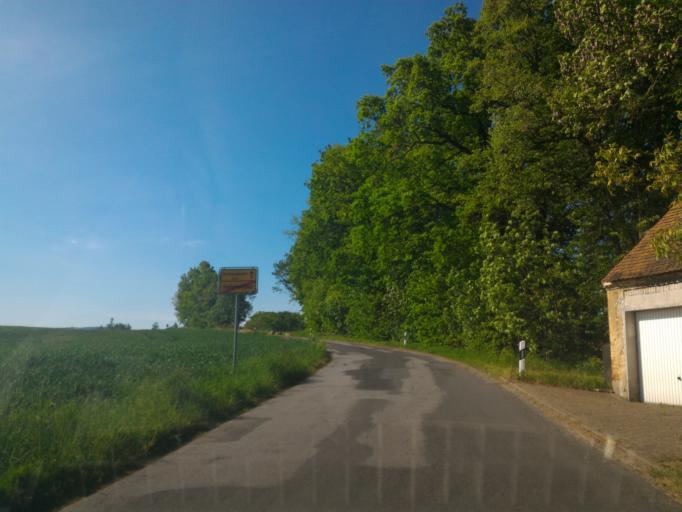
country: DE
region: Saxony
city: Grossschweidnitz
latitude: 51.0620
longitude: 14.6361
